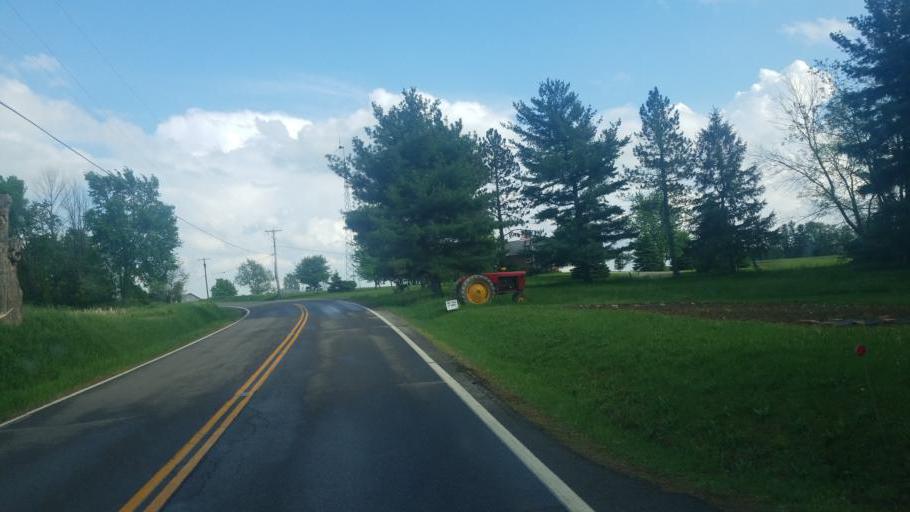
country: US
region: Ohio
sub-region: Ashland County
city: Ashland
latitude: 40.8741
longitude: -82.4132
